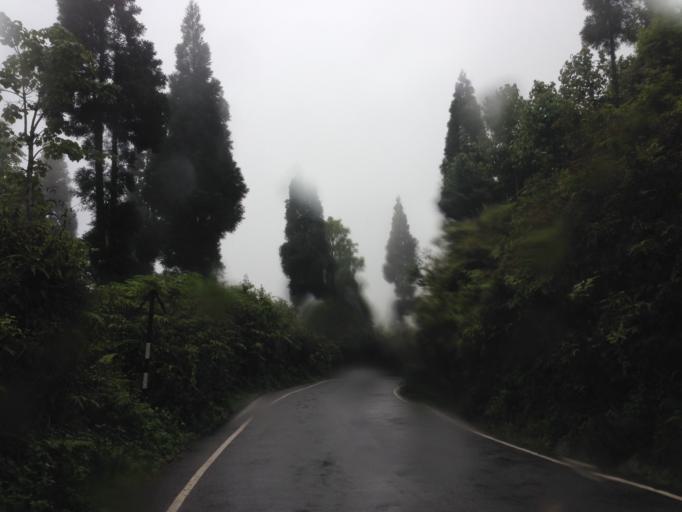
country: IN
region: West Bengal
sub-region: Darjiling
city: Mirik
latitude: 26.8815
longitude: 88.1880
